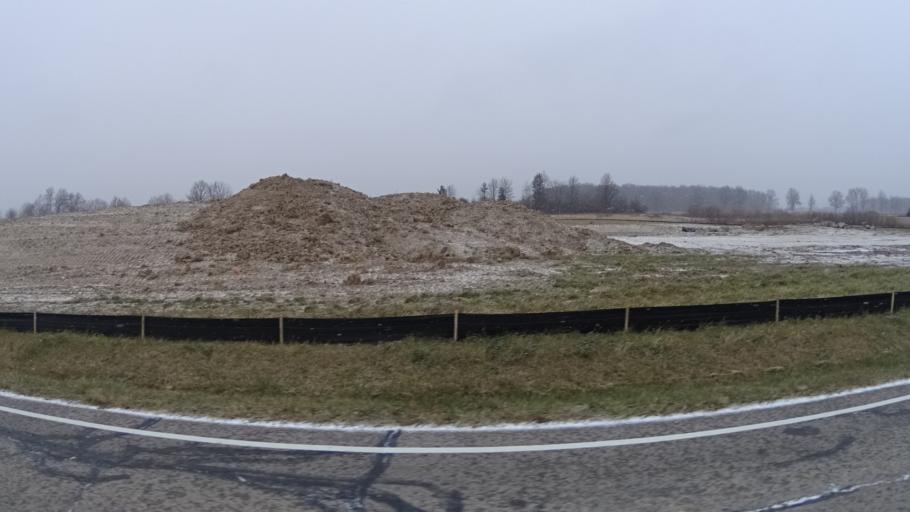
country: US
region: Ohio
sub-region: Lorain County
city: Oberlin
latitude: 41.3134
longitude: -82.1676
